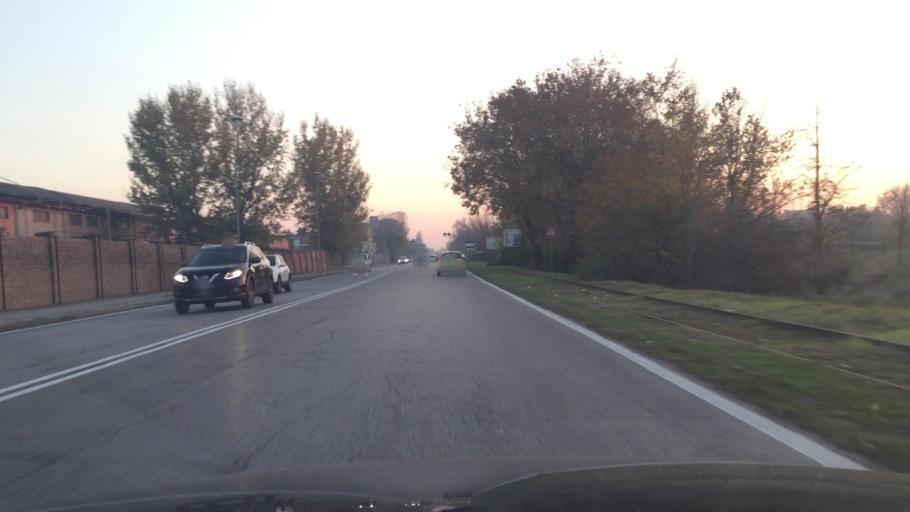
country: IT
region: Emilia-Romagna
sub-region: Provincia di Ferrara
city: Ferrara
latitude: 44.8568
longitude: 11.6009
